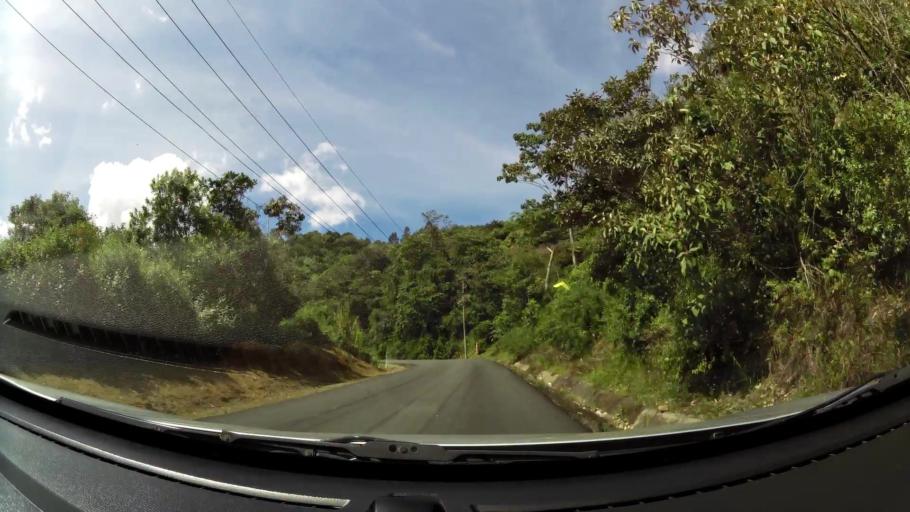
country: CR
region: San Jose
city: San Isidro
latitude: 9.3321
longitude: -83.7341
